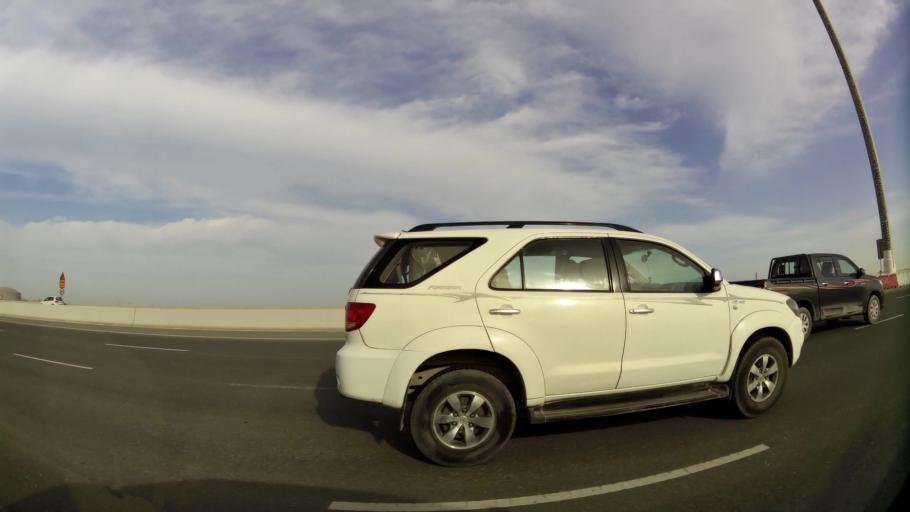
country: QA
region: Al Wakrah
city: Al Wakrah
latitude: 25.2304
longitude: 51.5925
